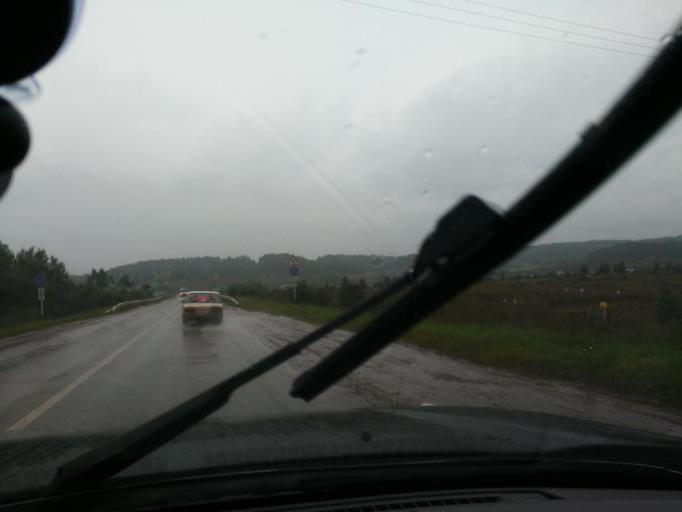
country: RU
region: Perm
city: Osa
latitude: 57.1954
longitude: 55.5918
